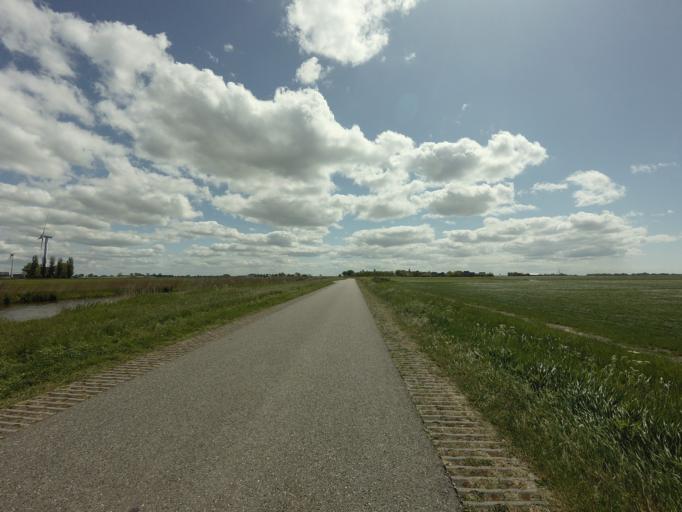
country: NL
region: Friesland
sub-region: Sudwest Fryslan
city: Makkum
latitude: 53.0904
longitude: 5.4162
